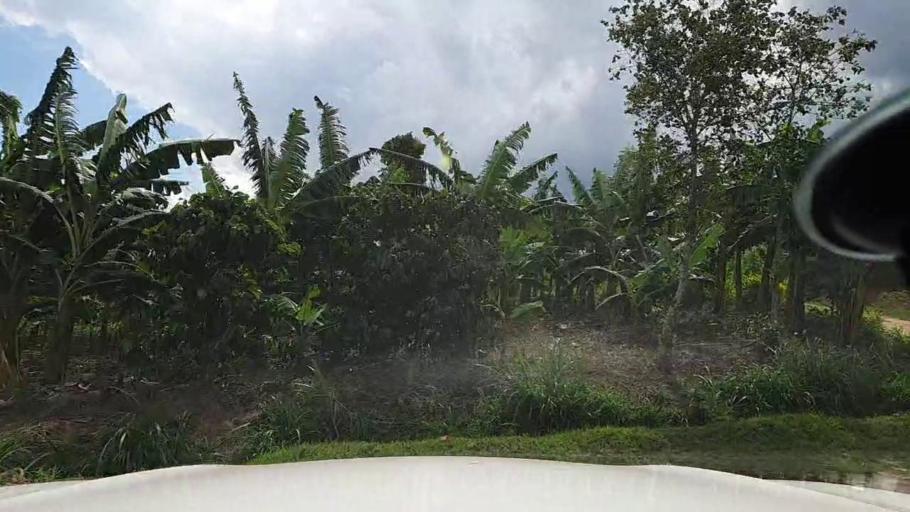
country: RW
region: Southern Province
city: Gitarama
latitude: -1.8203
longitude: 29.8001
